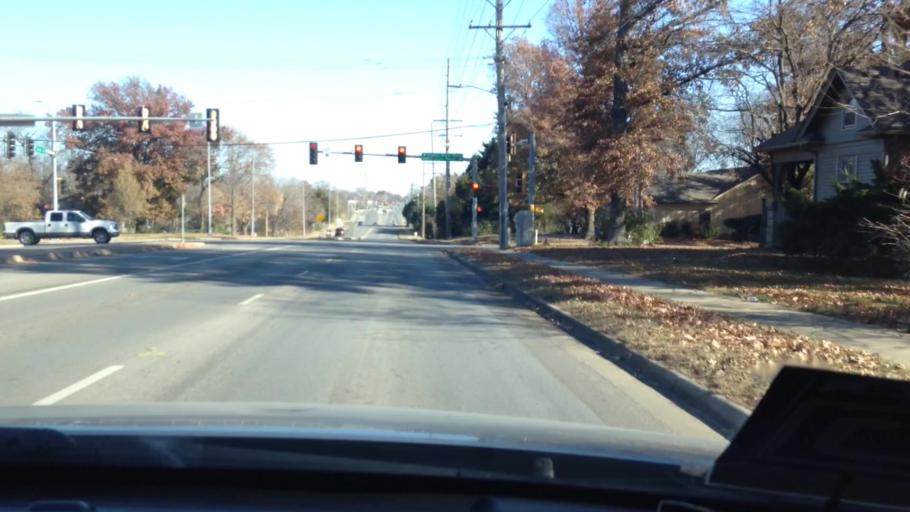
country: US
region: Kansas
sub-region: Johnson County
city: Olathe
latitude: 38.8837
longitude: -94.8444
